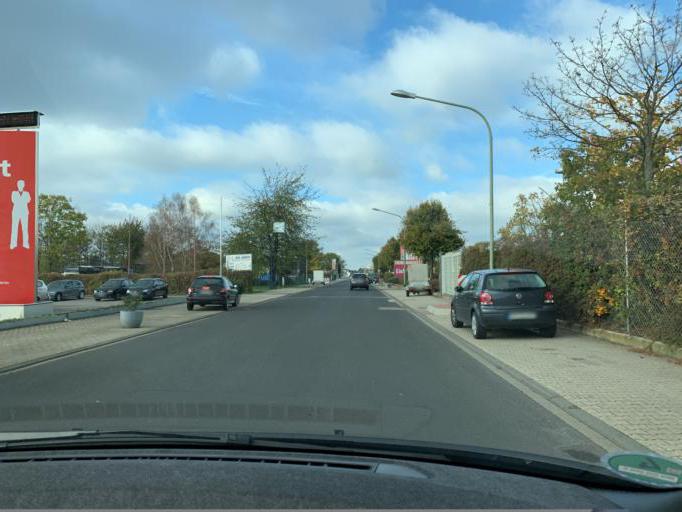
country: DE
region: North Rhine-Westphalia
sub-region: Regierungsbezirk Koln
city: Niederzier
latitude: 50.8436
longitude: 6.4534
